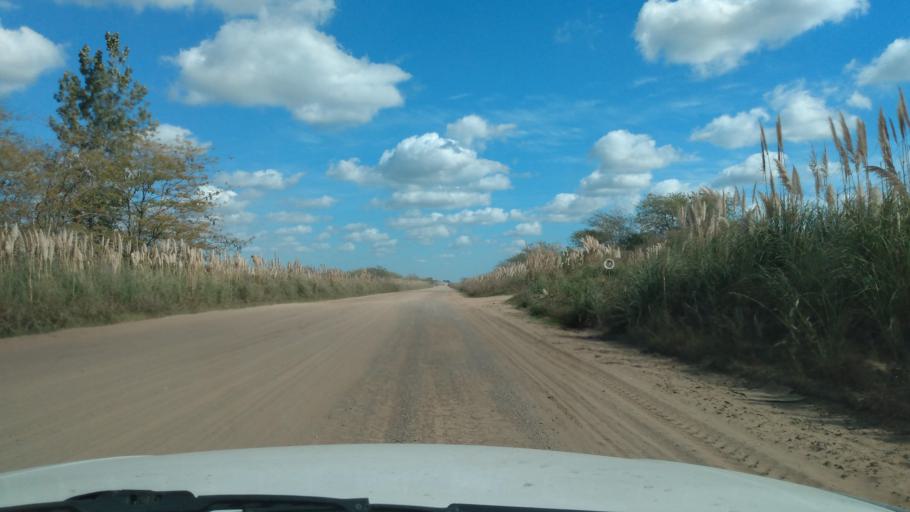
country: AR
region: Buenos Aires
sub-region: Partido de Navarro
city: Navarro
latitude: -35.0012
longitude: -59.3495
